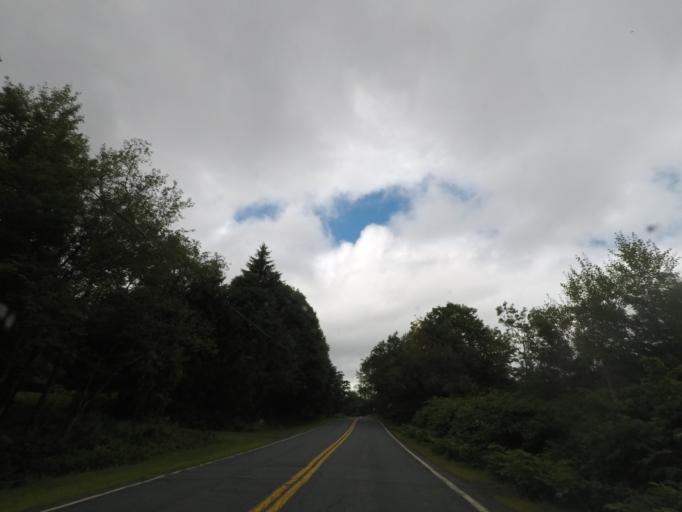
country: US
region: New York
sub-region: Rensselaer County
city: Poestenkill
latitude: 42.6905
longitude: -73.4552
